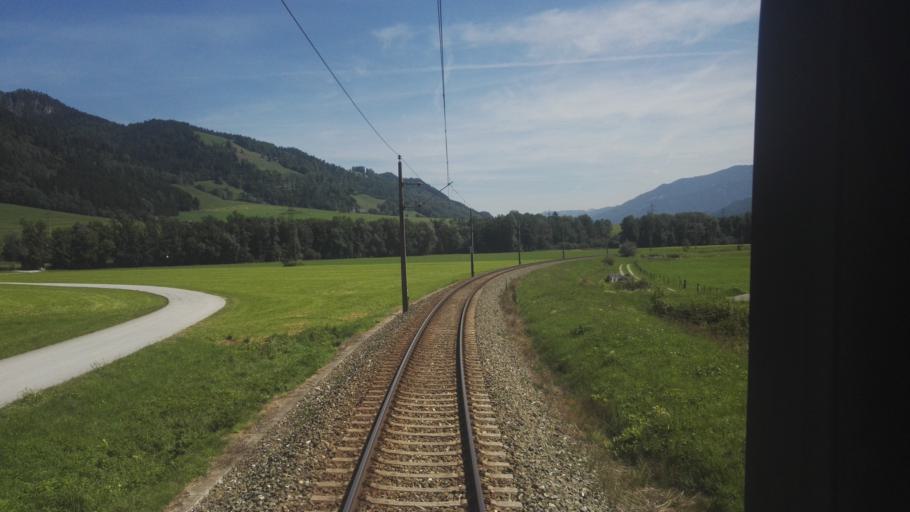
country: AT
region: Styria
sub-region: Politischer Bezirk Liezen
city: Pruggern
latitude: 47.4200
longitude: 13.8427
